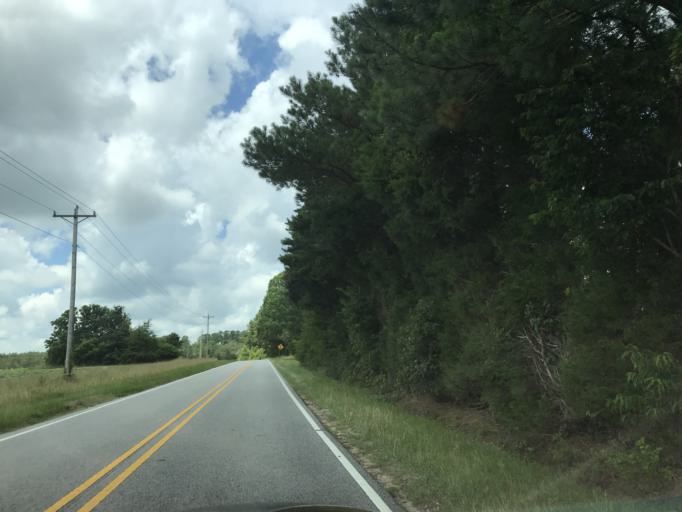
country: US
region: North Carolina
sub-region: Wake County
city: Rolesville
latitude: 35.9612
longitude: -78.4020
